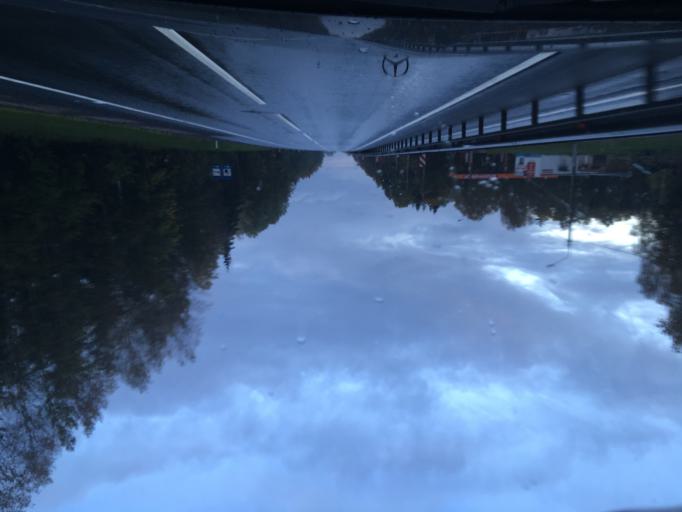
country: RU
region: Smolensk
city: Yartsevo
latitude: 55.0918
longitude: 32.8351
